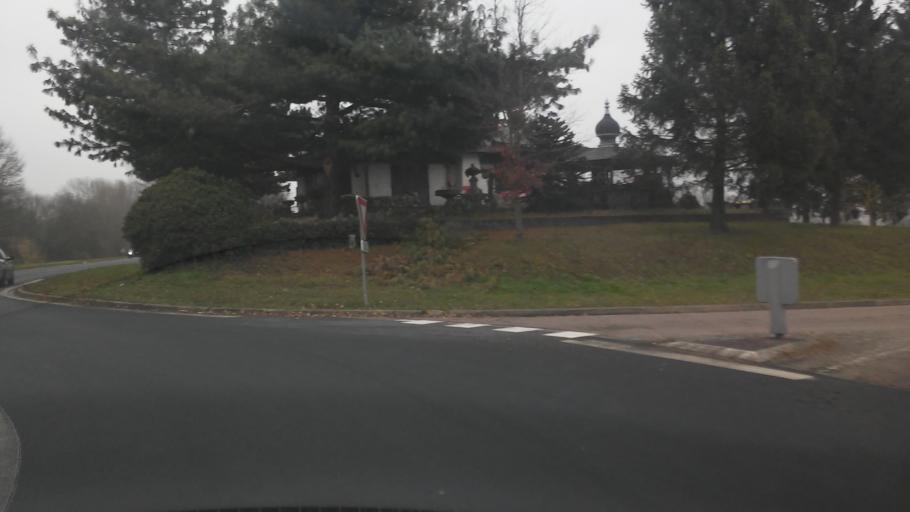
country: FR
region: Lorraine
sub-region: Departement de la Moselle
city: Marly
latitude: 49.0613
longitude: 6.1361
